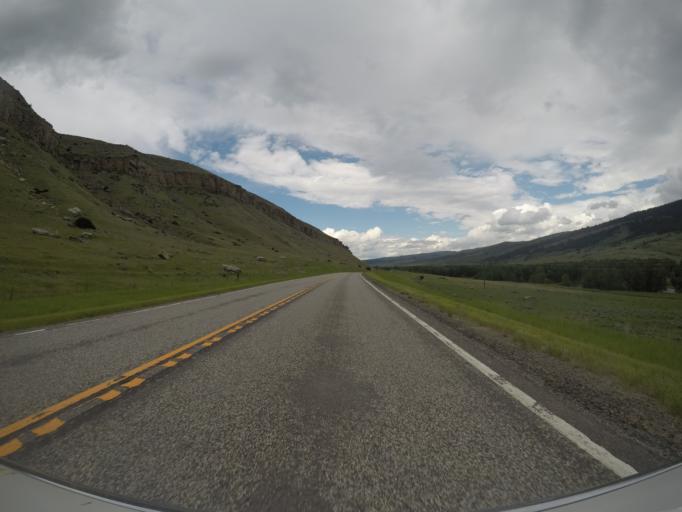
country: US
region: Montana
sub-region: Sweet Grass County
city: Big Timber
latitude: 45.5820
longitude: -110.1929
